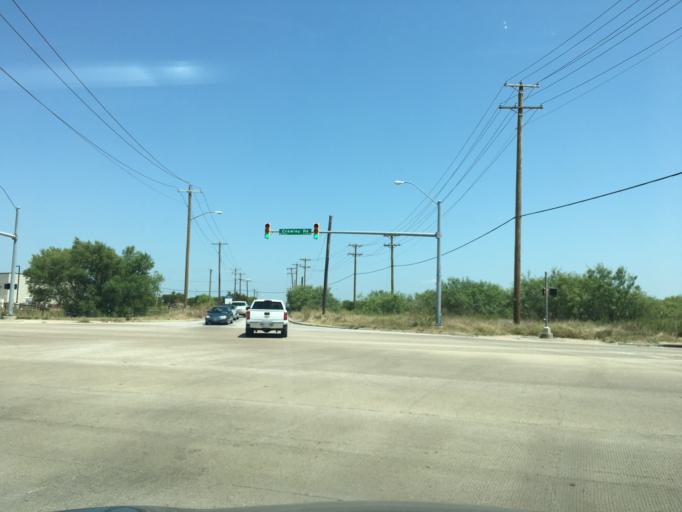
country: US
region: Texas
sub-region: Tarrant County
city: Crowley
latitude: 32.6142
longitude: -97.3502
